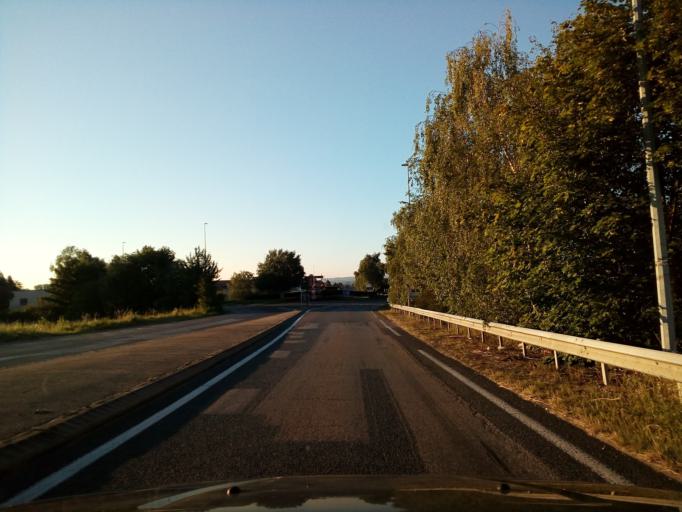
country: FR
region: Rhone-Alpes
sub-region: Departement de l'Isere
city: La Verpilliere
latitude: 45.6446
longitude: 5.1319
